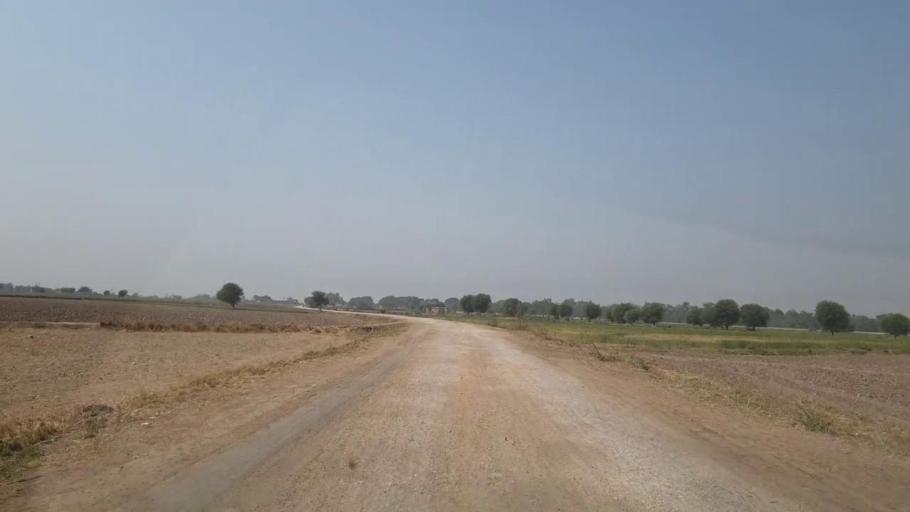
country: PK
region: Sindh
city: Mirpur Khas
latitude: 25.6511
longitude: 69.1064
